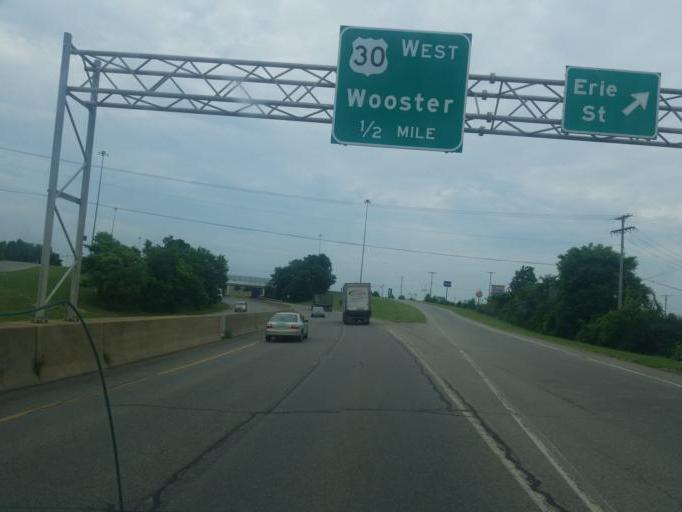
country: US
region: Ohio
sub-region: Stark County
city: Massillon
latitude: 40.7708
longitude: -81.5208
